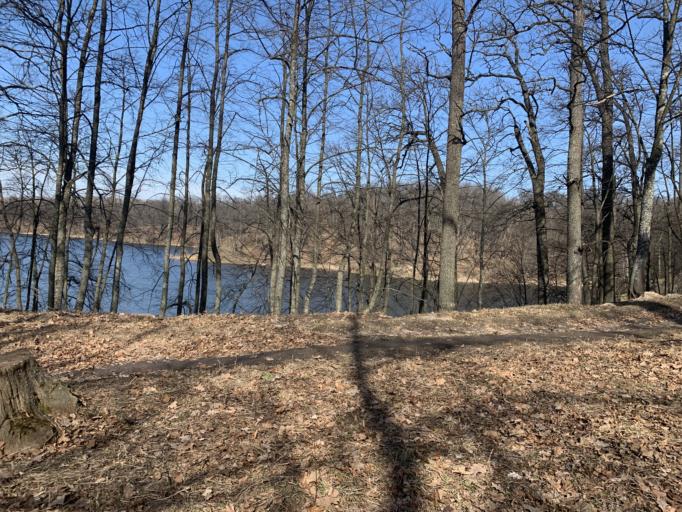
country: RU
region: Kursk
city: Zheleznogorsk
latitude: 52.3182
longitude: 35.3624
